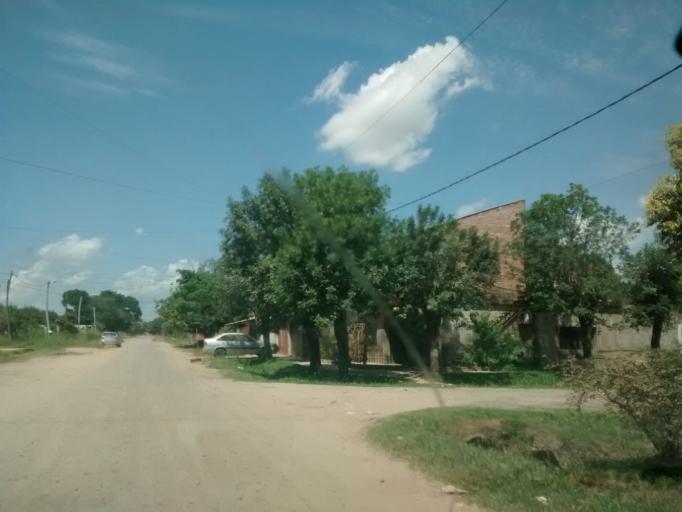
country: AR
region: Chaco
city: Resistencia
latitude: -27.4451
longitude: -58.9655
